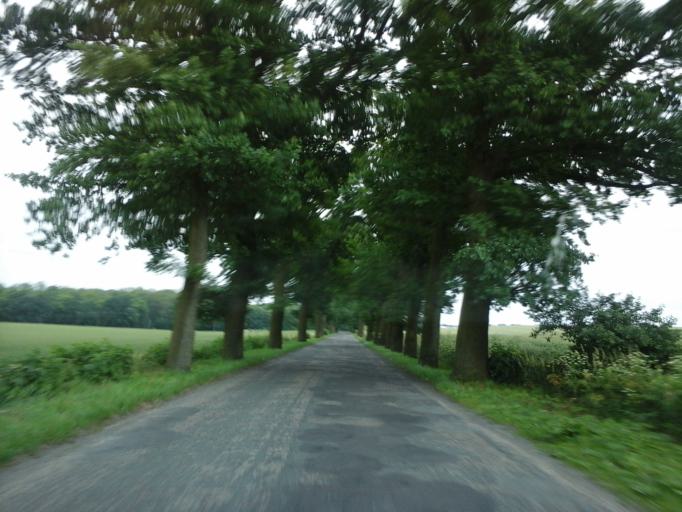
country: PL
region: West Pomeranian Voivodeship
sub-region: Powiat stargardzki
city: Dolice
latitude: 53.2637
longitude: 15.1669
